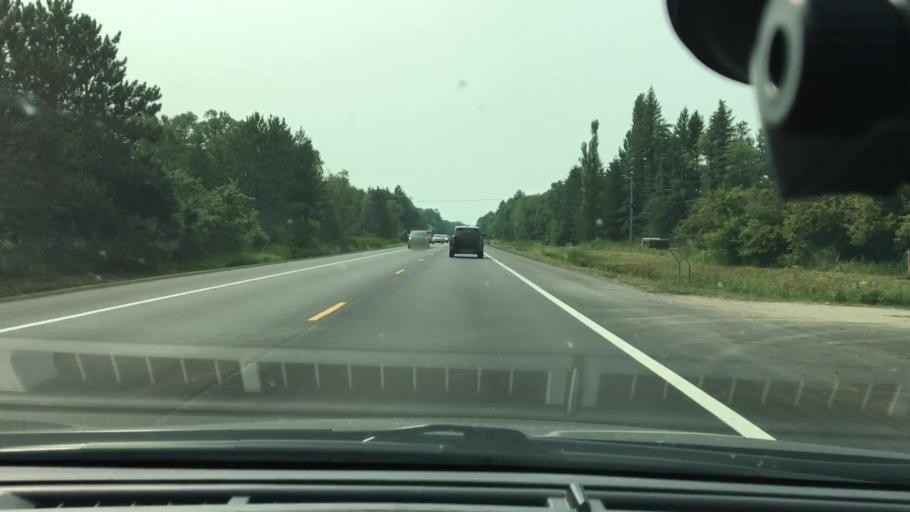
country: US
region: Minnesota
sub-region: Crow Wing County
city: Brainerd
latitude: 46.4470
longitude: -94.1719
